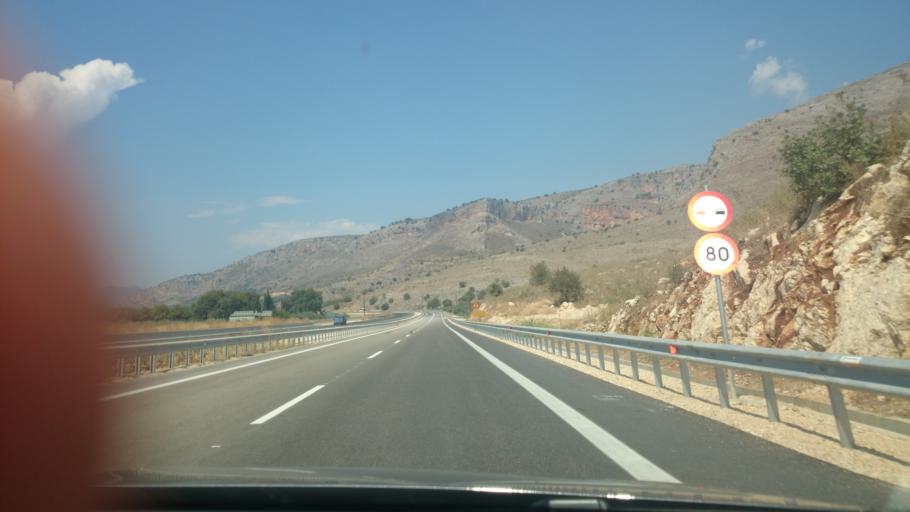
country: GR
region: West Greece
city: Aitoliko
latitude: 38.4225
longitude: 21.3883
